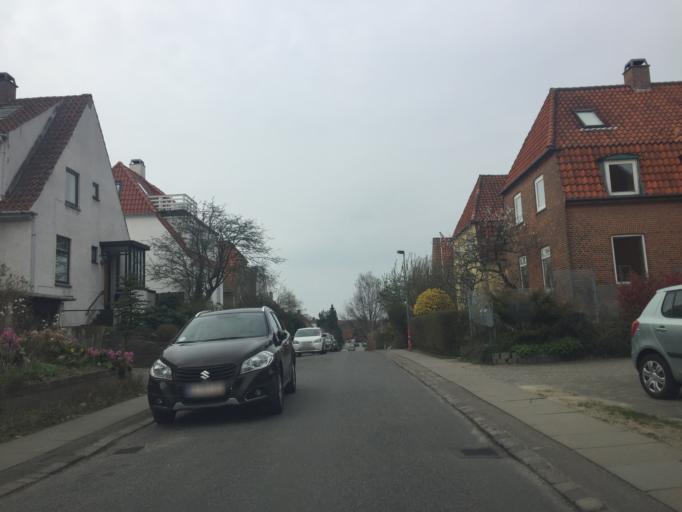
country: DK
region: Capital Region
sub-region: Kobenhavn
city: Vanlose
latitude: 55.7078
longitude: 12.5053
